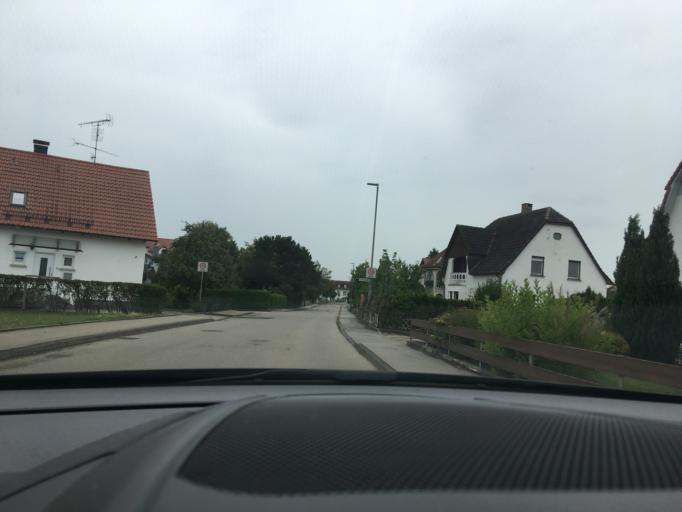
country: DE
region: Baden-Wuerttemberg
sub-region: Tuebingen Region
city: Kirchdorf
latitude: 48.0748
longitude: 10.1275
